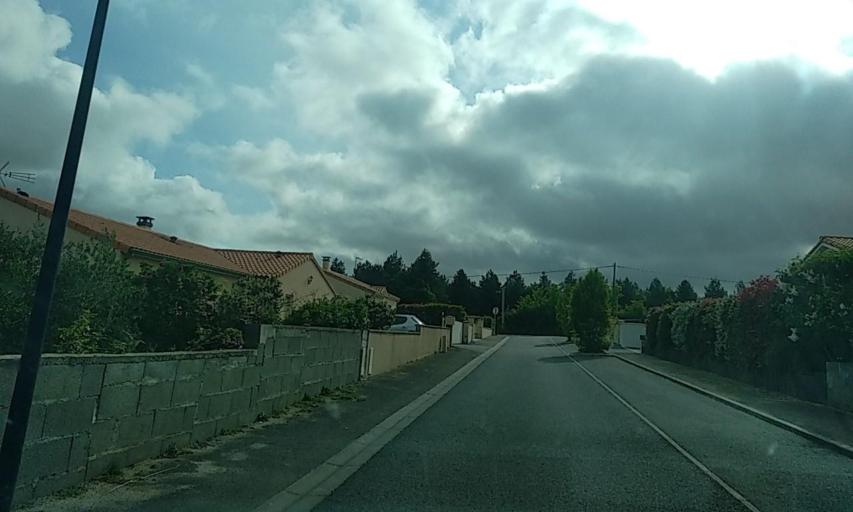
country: FR
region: Poitou-Charentes
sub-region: Departement des Deux-Sevres
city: Boisme
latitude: 46.7695
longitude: -0.4297
